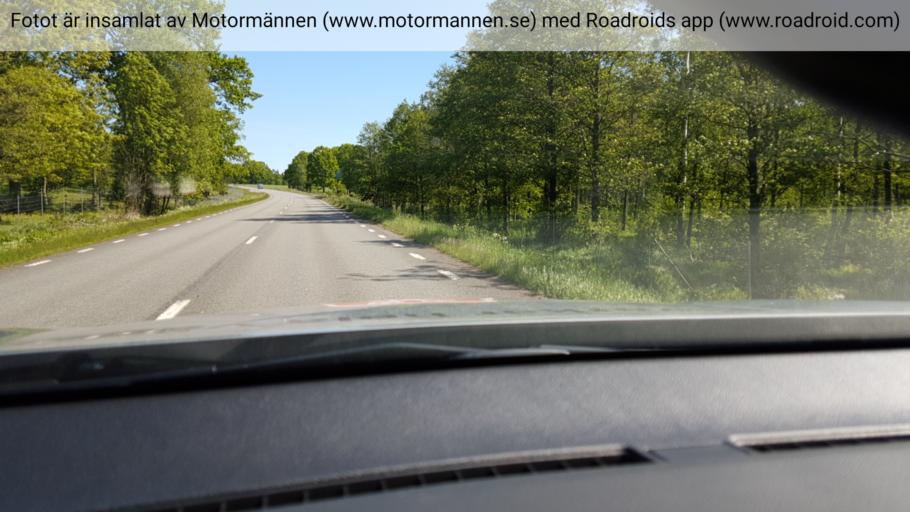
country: SE
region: Vaestra Goetaland
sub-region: Hjo Kommun
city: Hjo
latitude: 58.3461
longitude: 14.3456
